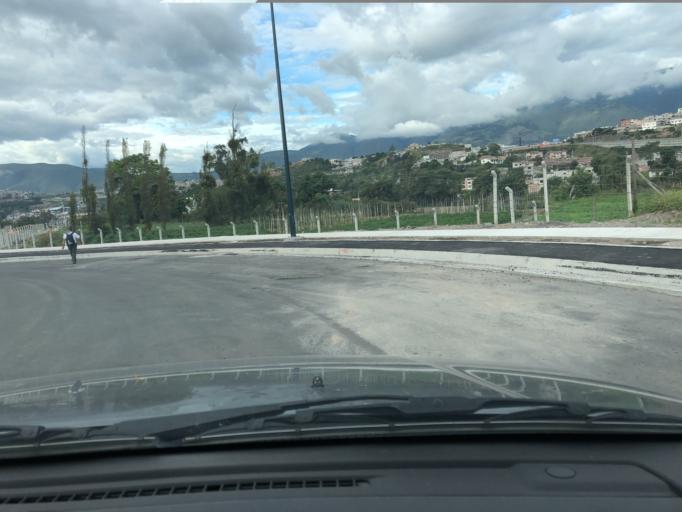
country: EC
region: Imbabura
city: Ibarra
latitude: 0.3399
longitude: -78.1549
